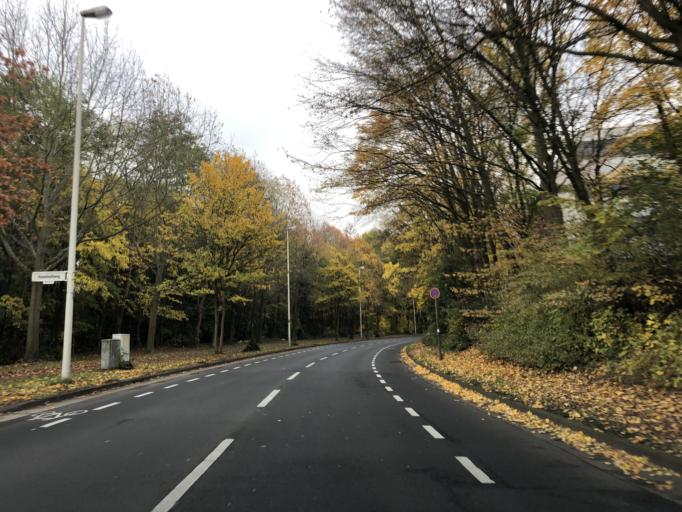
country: DE
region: North Rhine-Westphalia
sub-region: Regierungsbezirk Koln
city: Konigswinter
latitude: 50.6659
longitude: 7.1540
